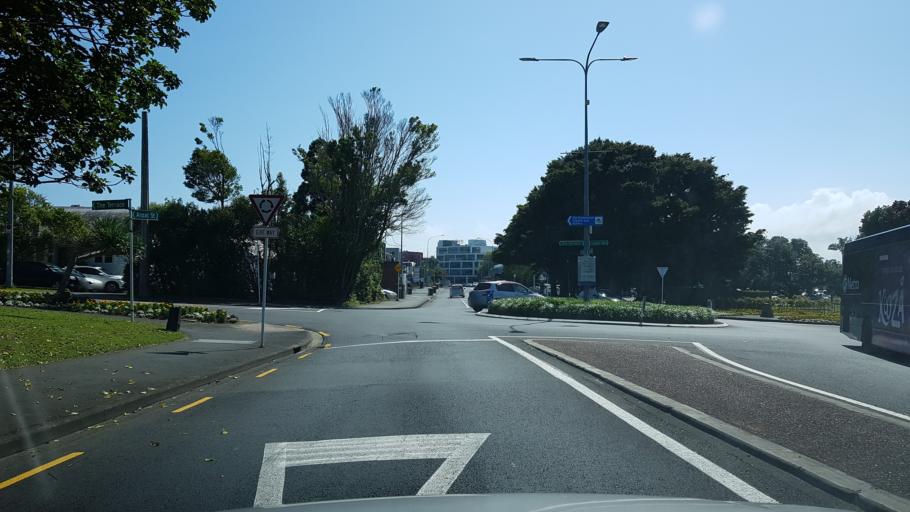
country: NZ
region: Auckland
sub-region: Auckland
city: North Shore
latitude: -36.7872
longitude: 174.7702
